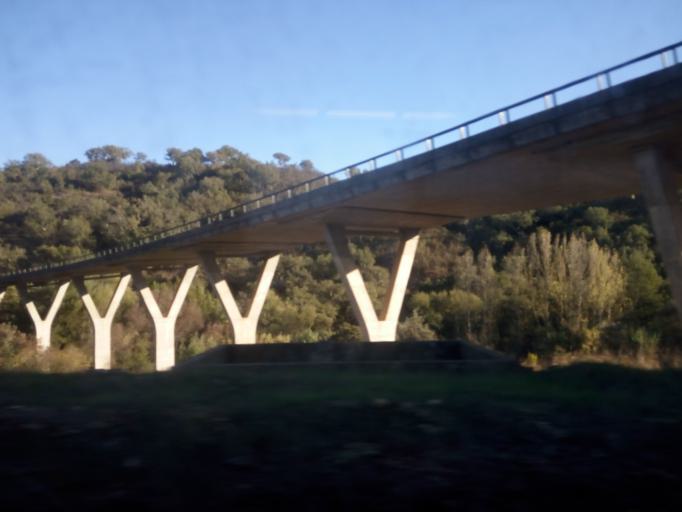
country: PT
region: Beja
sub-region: Odemira
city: Odemira
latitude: 37.5868
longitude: -8.4911
